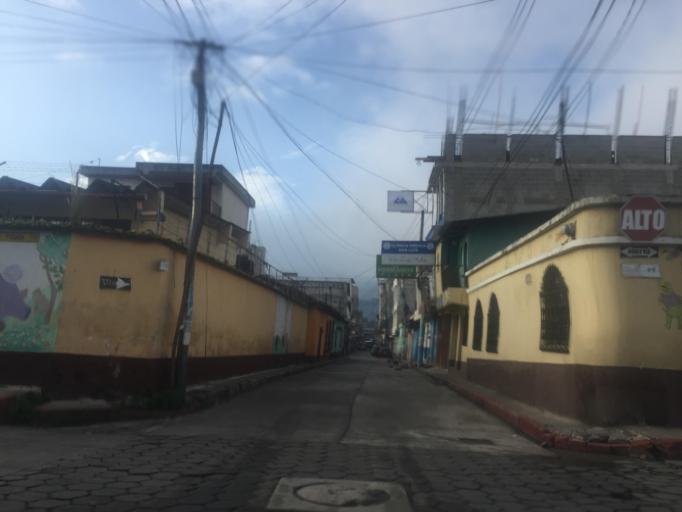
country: GT
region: Totonicapan
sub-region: Municipio de Totonicapan
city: Totonicapan
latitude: 14.9134
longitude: -91.3620
